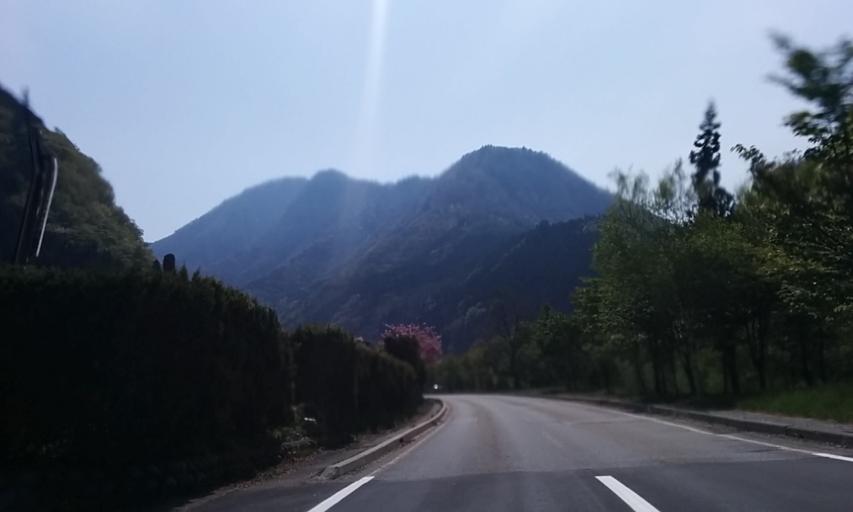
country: JP
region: Gifu
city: Takayama
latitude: 36.2459
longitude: 137.5227
